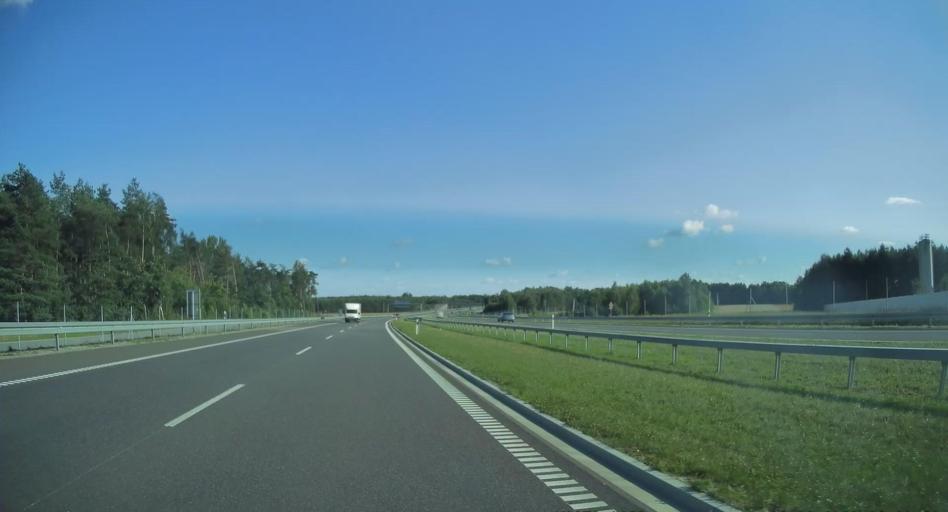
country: PL
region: Masovian Voivodeship
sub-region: Powiat radomski
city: Jedlinsk
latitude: 51.5290
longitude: 21.0823
